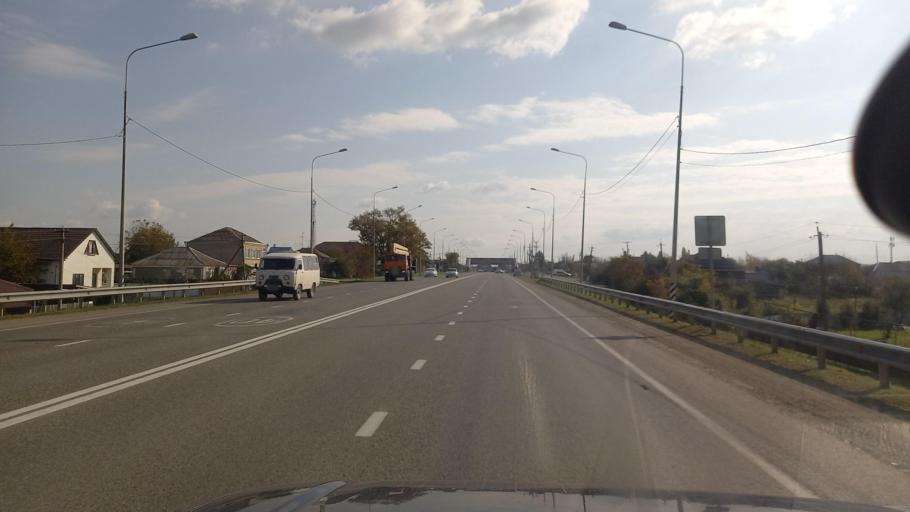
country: RU
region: Krasnodarskiy
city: Novoukrainskiy
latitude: 44.8976
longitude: 38.0450
